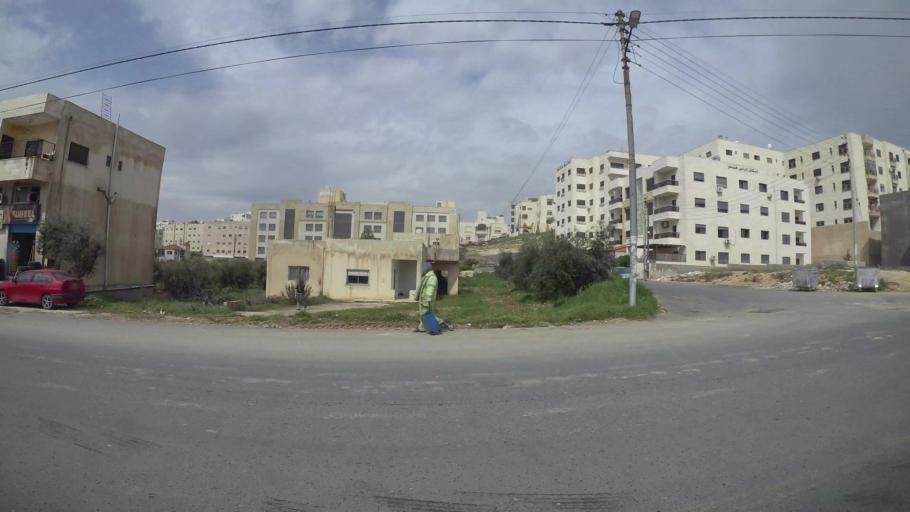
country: JO
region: Amman
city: Umm as Summaq
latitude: 31.9099
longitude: 35.8495
